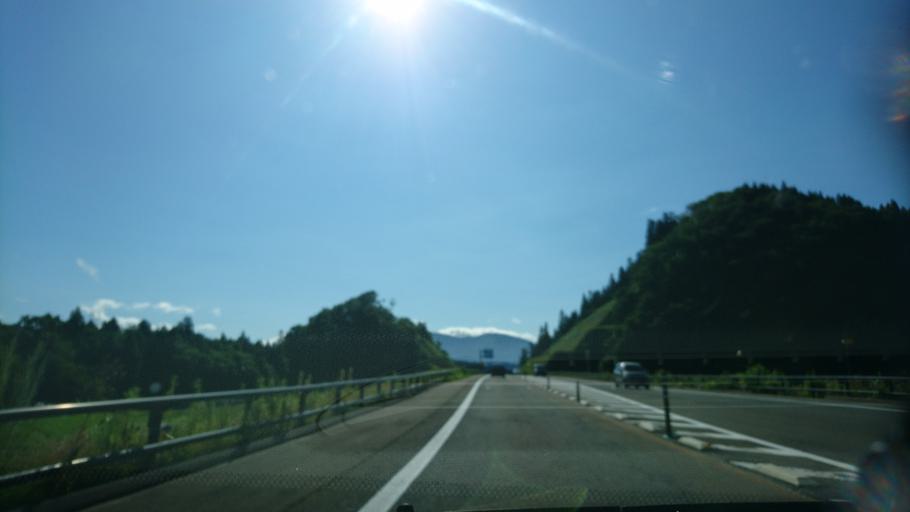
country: JP
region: Akita
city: Kakunodatemachi
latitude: 39.5957
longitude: 140.5308
